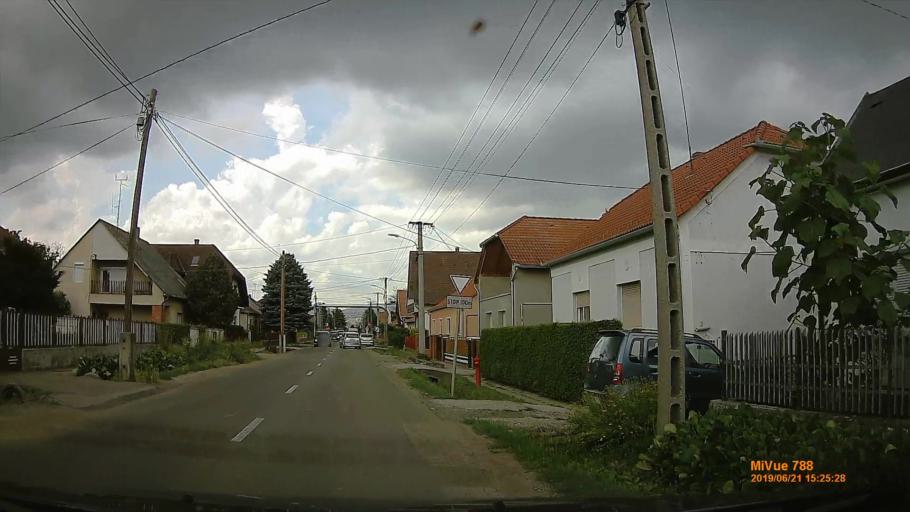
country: HU
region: Baranya
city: Pecs
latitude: 46.0448
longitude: 18.2484
